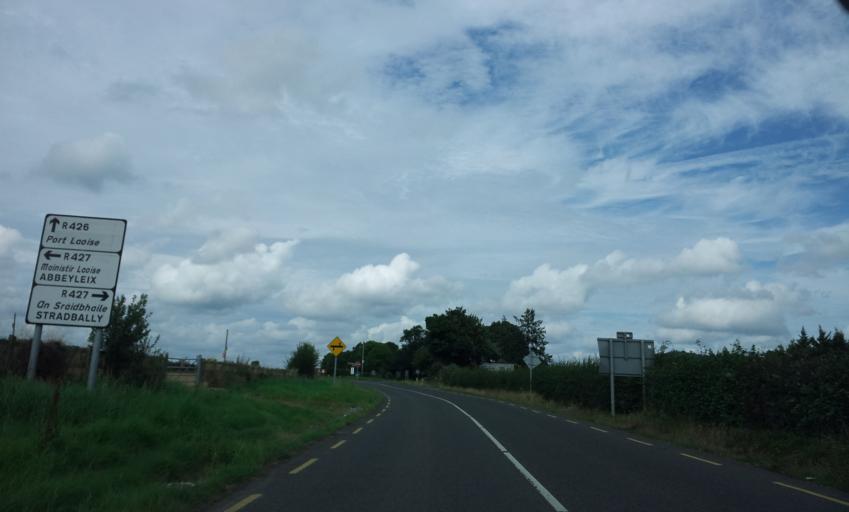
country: IE
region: Leinster
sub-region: Laois
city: Stradbally
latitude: 52.9948
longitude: -7.2215
